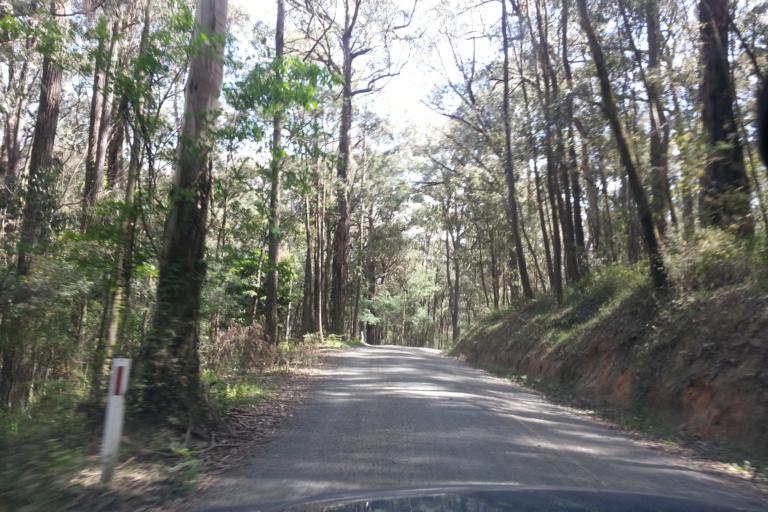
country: AU
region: Victoria
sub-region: Cardinia
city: Gembrook
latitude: -37.9498
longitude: 145.5797
